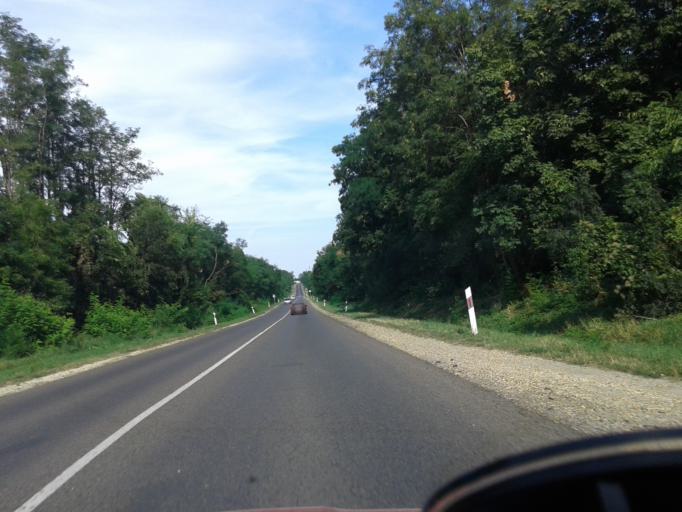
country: HU
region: Pest
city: Godollo
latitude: 47.5900
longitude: 19.3147
